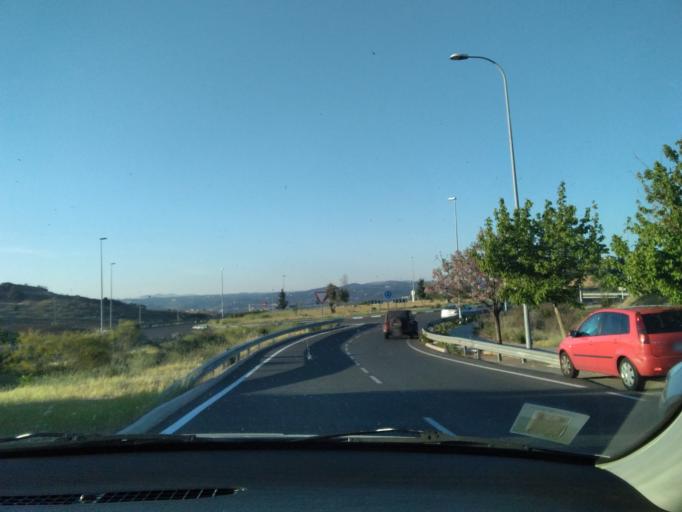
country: ES
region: Castille-La Mancha
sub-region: Province of Toledo
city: Toledo
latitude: 39.8887
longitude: -4.0554
